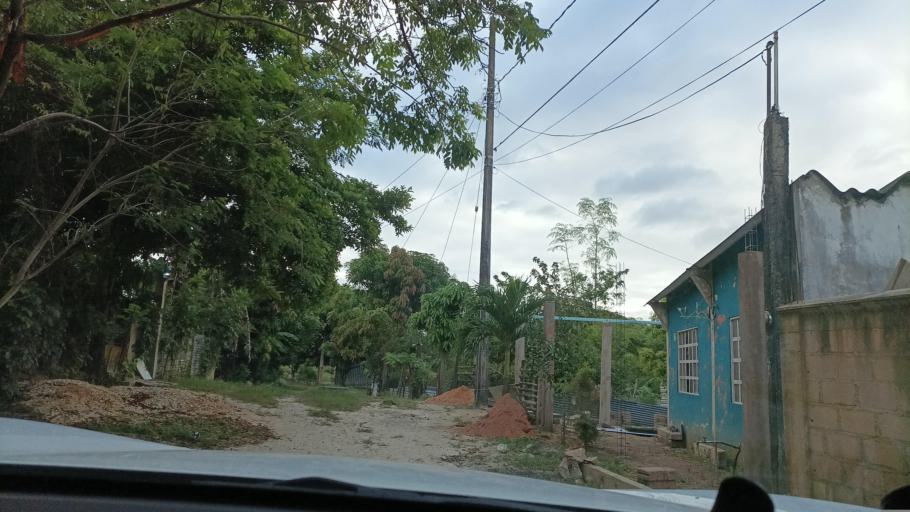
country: MX
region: Veracruz
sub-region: Cosoleacaque
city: Hermenegildo J. Aldana
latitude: 17.9933
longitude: -94.6100
